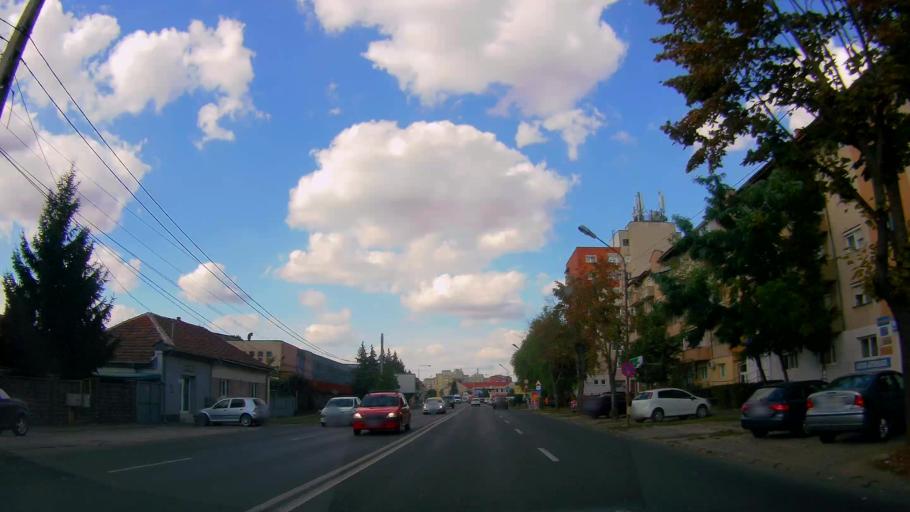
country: RO
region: Satu Mare
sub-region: Municipiul Satu Mare
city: Satu Mare
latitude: 47.7745
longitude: 22.8838
